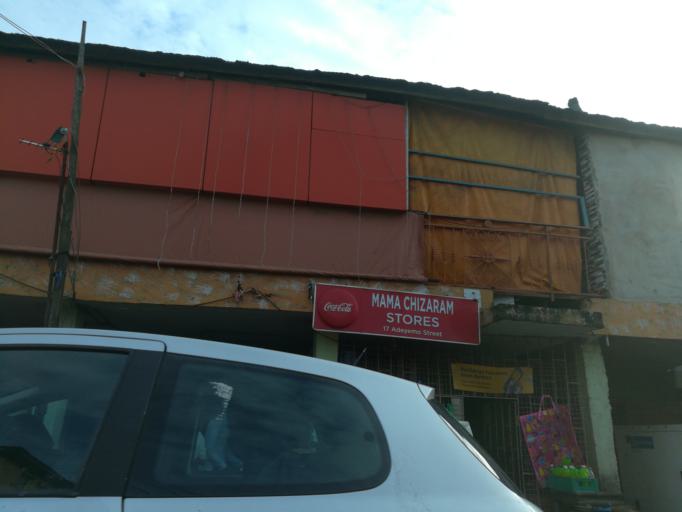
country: NG
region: Lagos
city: Oshodi
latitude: 6.5530
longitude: 3.3321
